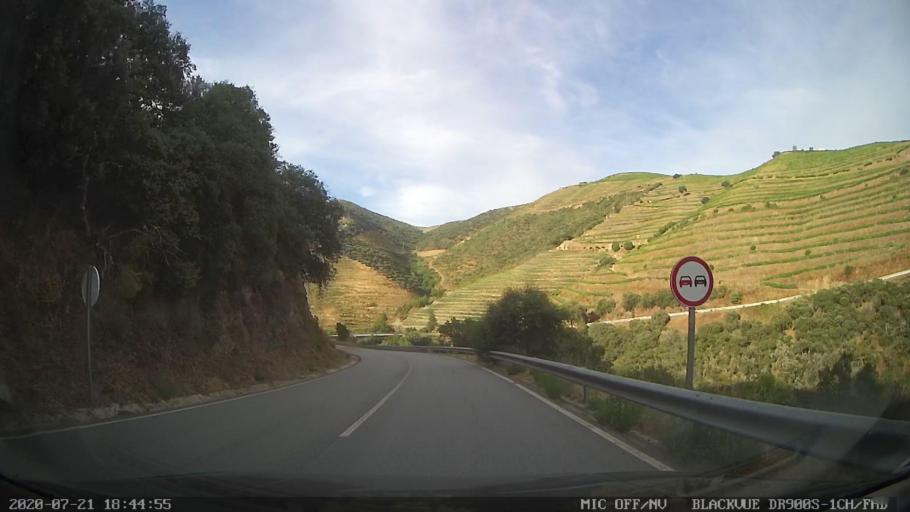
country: PT
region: Viseu
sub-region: Sao Joao da Pesqueira
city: Sao Joao da Pesqueira
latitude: 41.1209
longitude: -7.4514
